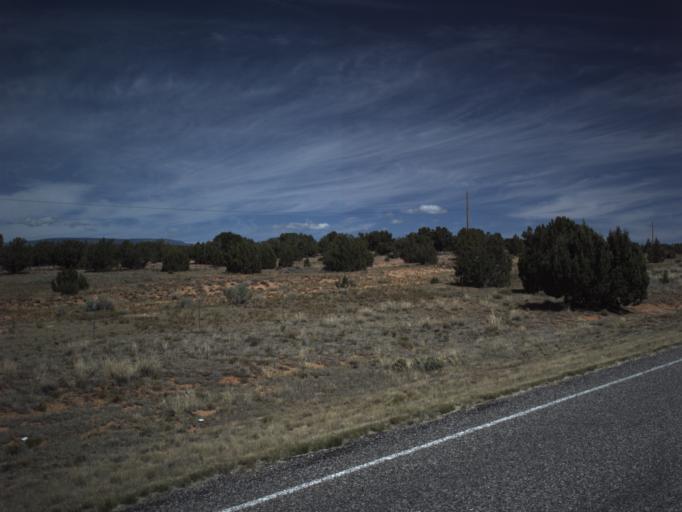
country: US
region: Utah
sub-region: Wayne County
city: Loa
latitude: 37.7361
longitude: -111.5107
